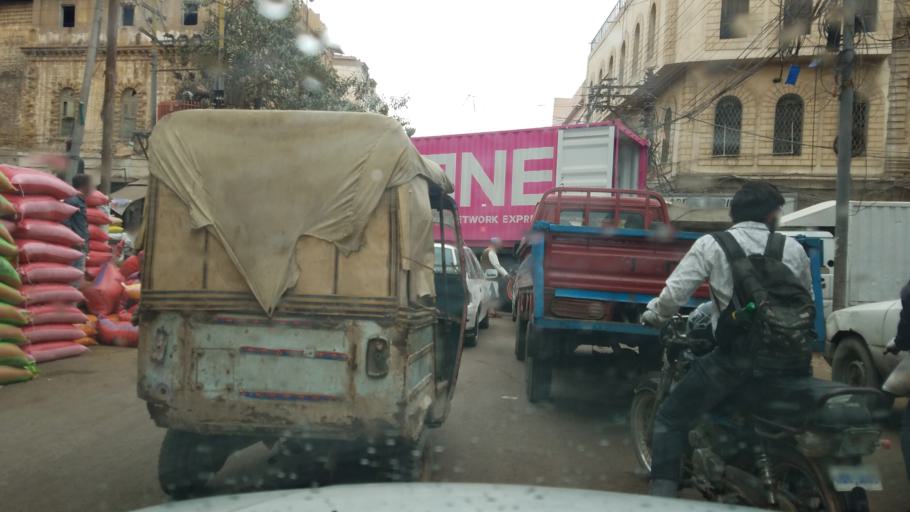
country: PK
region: Sindh
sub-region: Karachi District
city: Karachi
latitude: 24.8557
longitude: 67.0043
